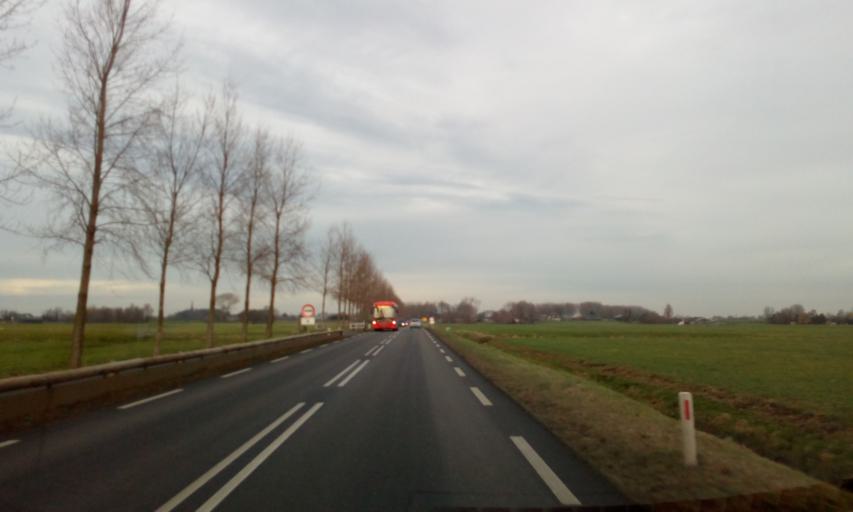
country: NL
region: South Holland
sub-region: Gemeente Zoetermeer
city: Zoetermeer
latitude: 52.0846
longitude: 4.4747
